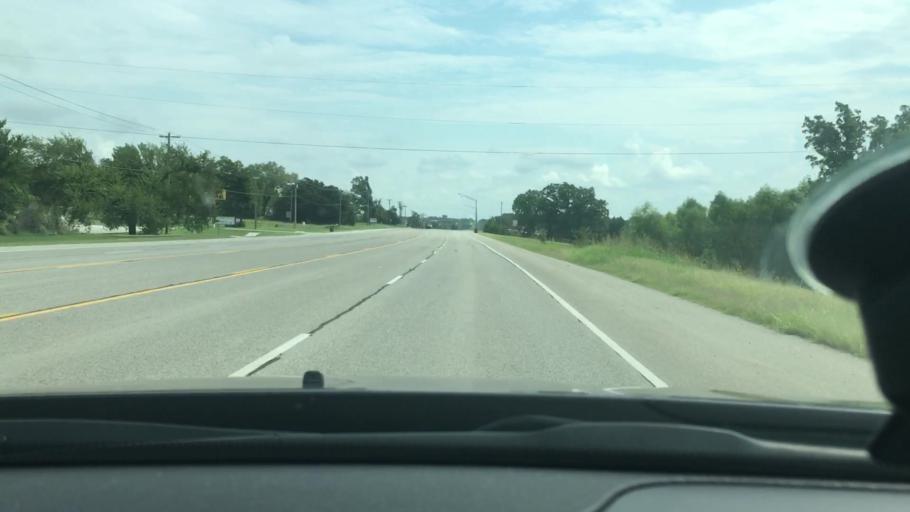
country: US
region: Oklahoma
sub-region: Carter County
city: Dickson
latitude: 34.1871
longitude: -96.9914
